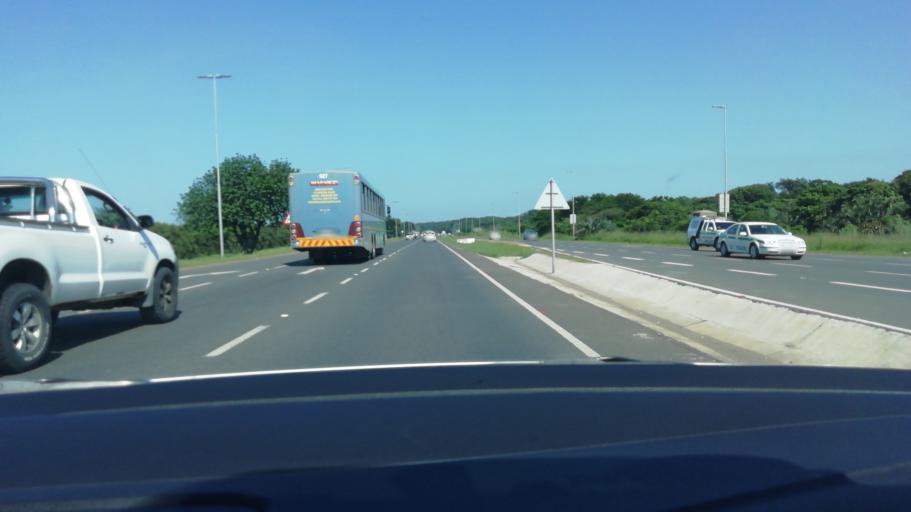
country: ZA
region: KwaZulu-Natal
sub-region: uThungulu District Municipality
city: Richards Bay
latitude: -28.7718
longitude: 32.0668
